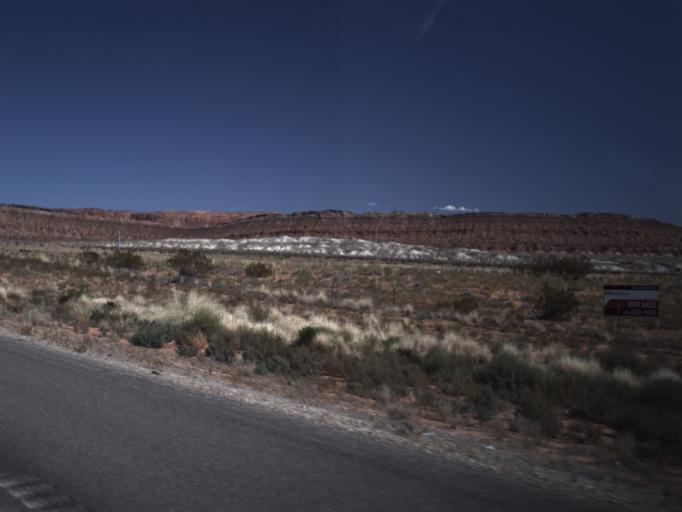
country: US
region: Utah
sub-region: Washington County
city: Washington
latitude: 37.0235
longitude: -113.4861
